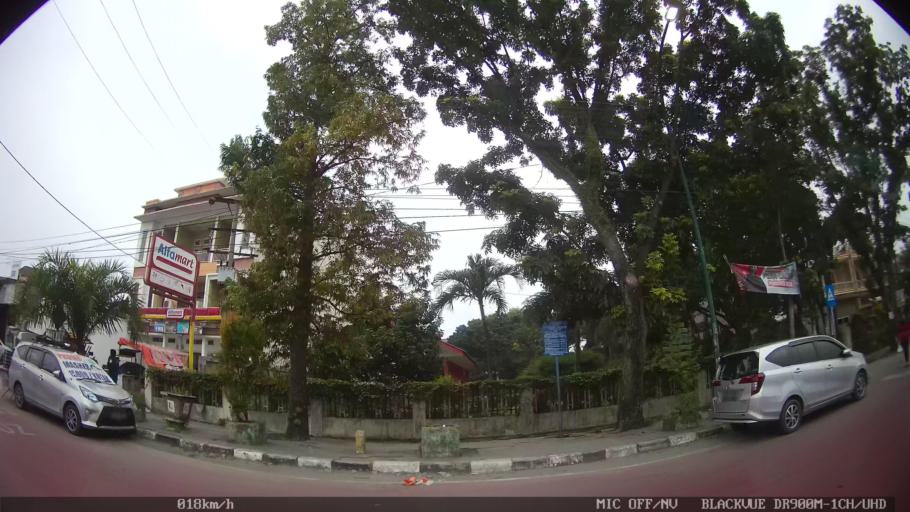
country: ID
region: North Sumatra
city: Medan
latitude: 3.5684
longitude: 98.7023
